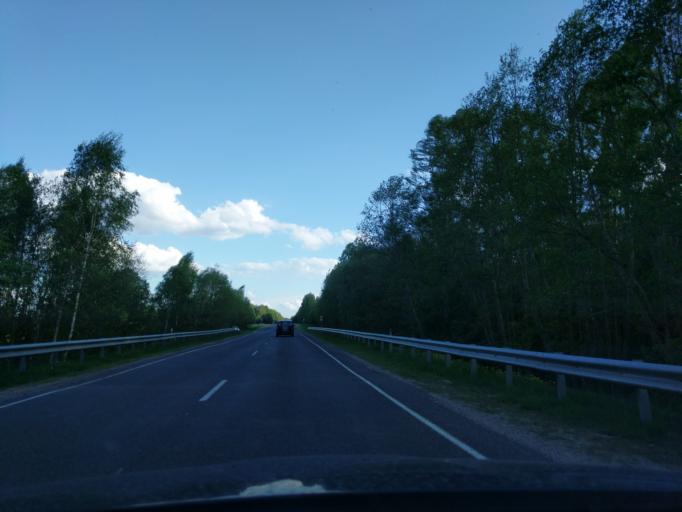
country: BY
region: Minsk
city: Kryvichy
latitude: 54.6089
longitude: 27.1799
